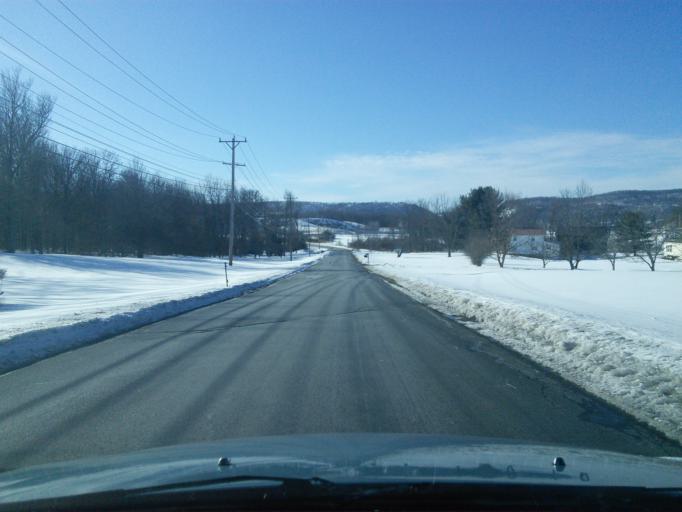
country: US
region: Pennsylvania
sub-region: Centre County
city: Park Forest Village
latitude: 40.8153
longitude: -77.9348
